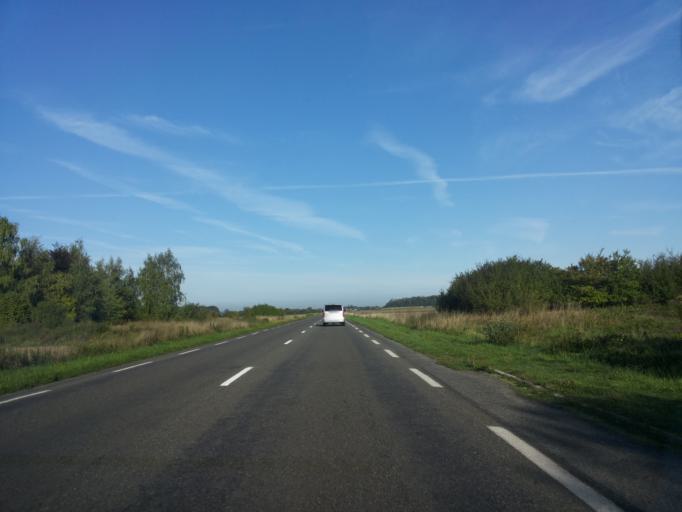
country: FR
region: Picardie
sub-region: Departement de l'Aisne
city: Athies-sous-Laon
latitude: 49.5542
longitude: 3.7120
